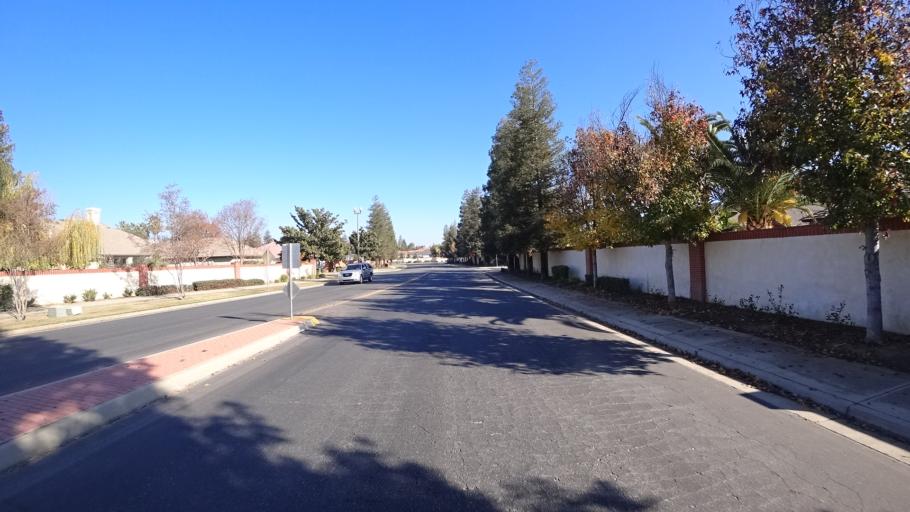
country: US
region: California
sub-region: Kern County
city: Greenacres
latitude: 35.3309
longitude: -119.1268
